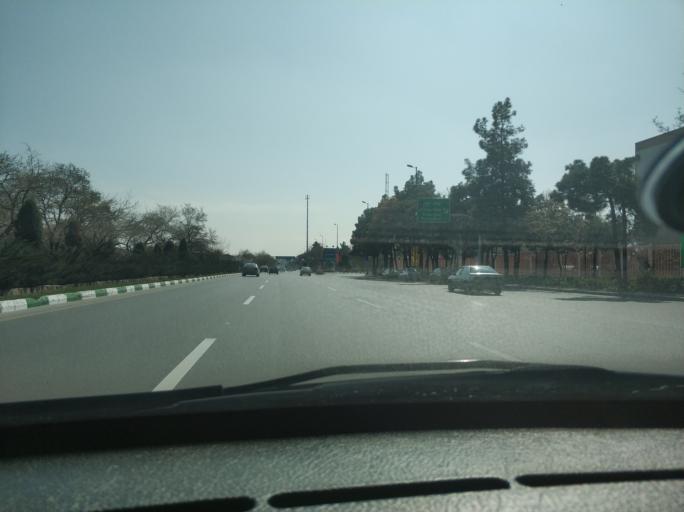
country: IR
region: Razavi Khorasan
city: Mashhad
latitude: 36.3203
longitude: 59.5234
